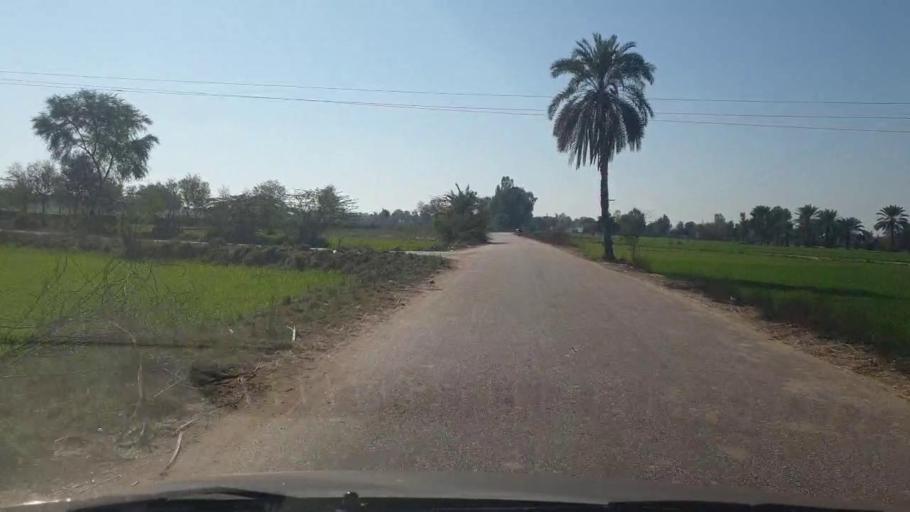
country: PK
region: Sindh
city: Bozdar
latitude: 27.1000
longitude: 68.6299
